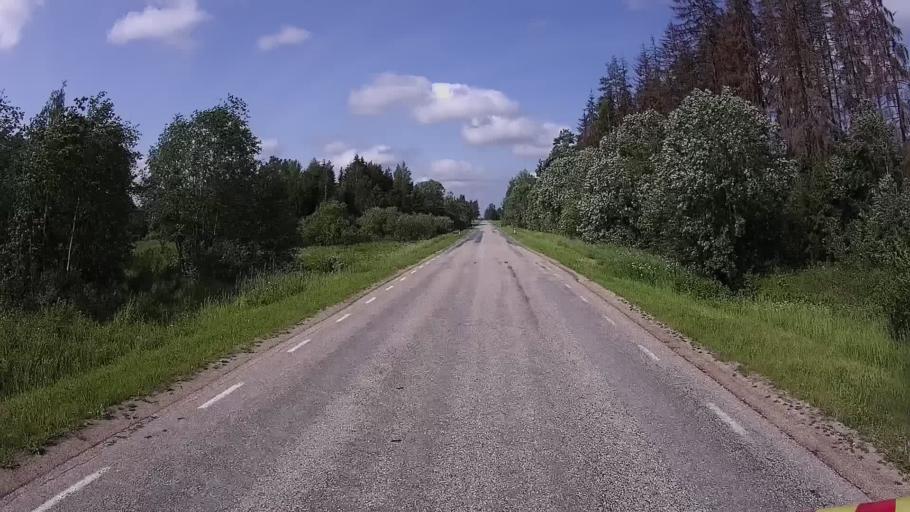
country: EE
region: Vorumaa
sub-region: Antsla vald
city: Vana-Antsla
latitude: 57.8471
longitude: 26.5695
